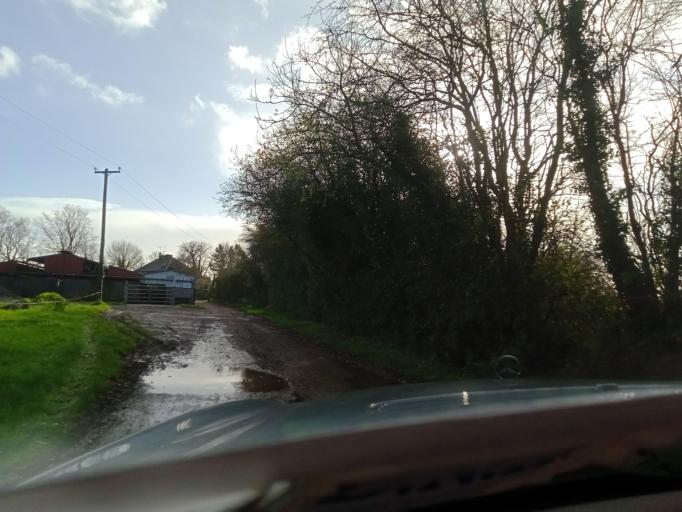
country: IE
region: Leinster
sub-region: Kilkenny
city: Mooncoin
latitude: 52.3247
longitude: -7.2743
